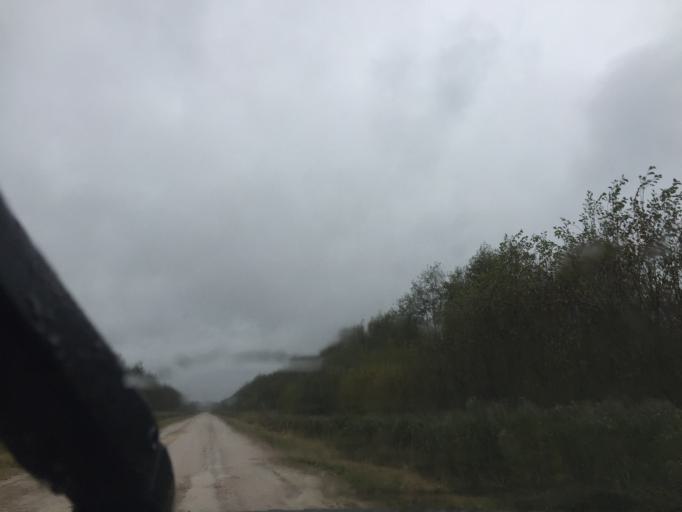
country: LV
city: Tireli
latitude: 56.7469
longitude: 23.5280
